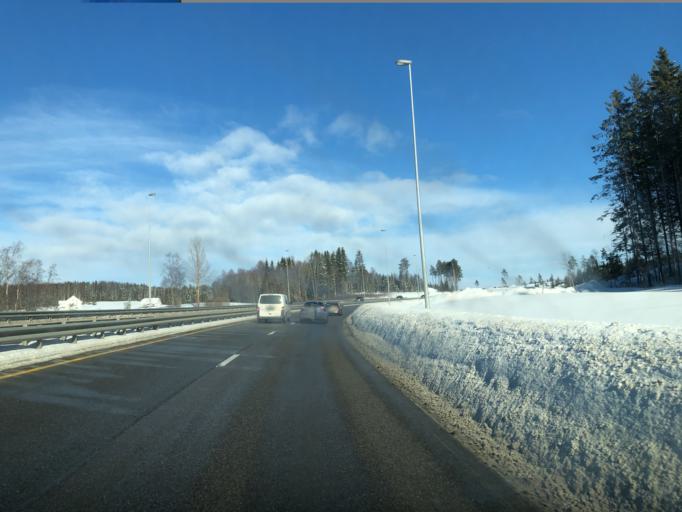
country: NO
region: Oppland
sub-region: Gran
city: Jaren
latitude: 60.4328
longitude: 10.5842
